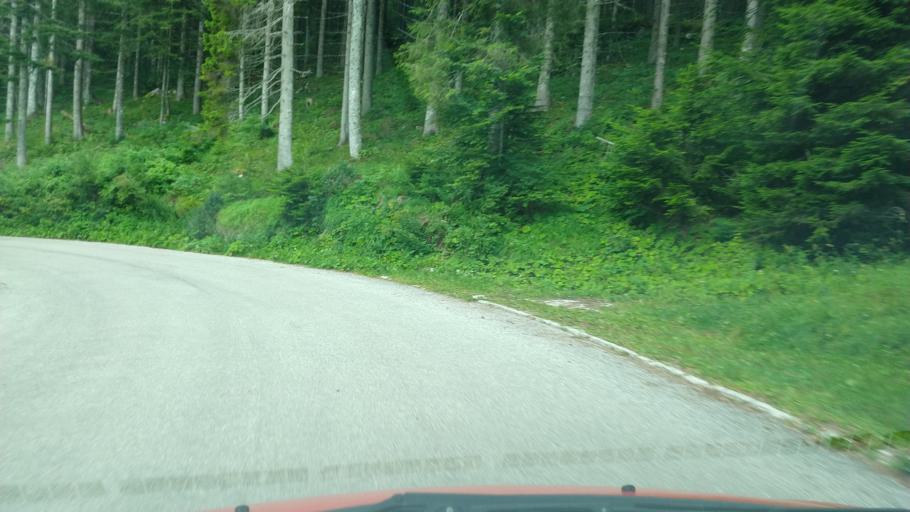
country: IT
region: Veneto
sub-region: Provincia di Vicenza
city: Lastebasse
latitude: 45.8930
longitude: 11.2732
